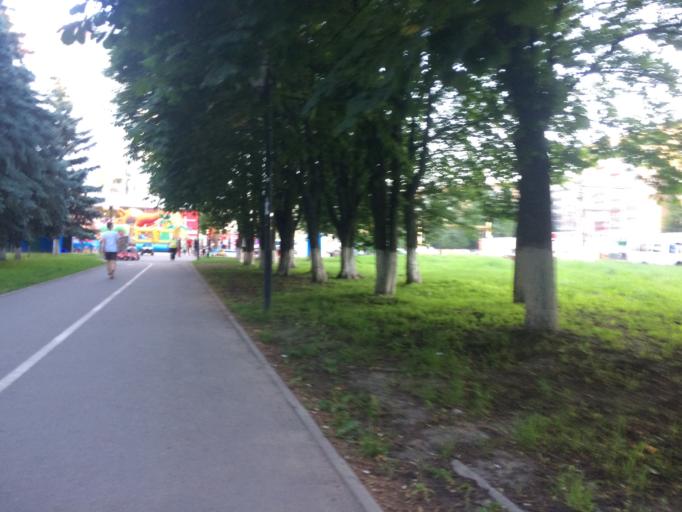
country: RU
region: Kursk
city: Kursk
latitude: 51.6684
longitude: 36.1417
